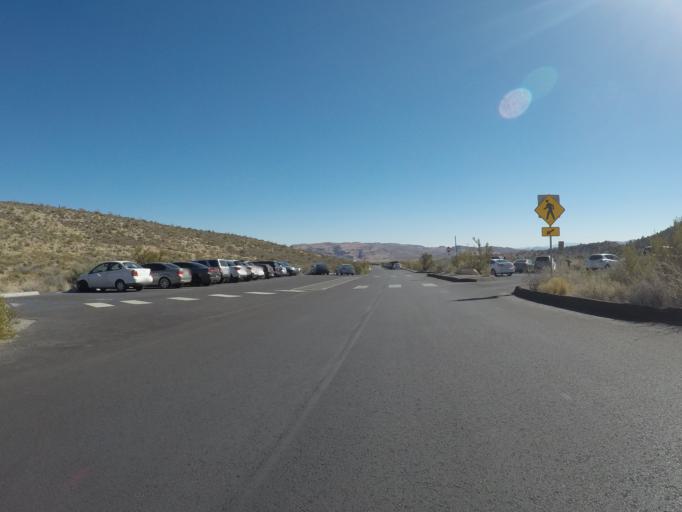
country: US
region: Nevada
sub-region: Clark County
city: Summerlin South
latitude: 36.1504
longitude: -115.4843
